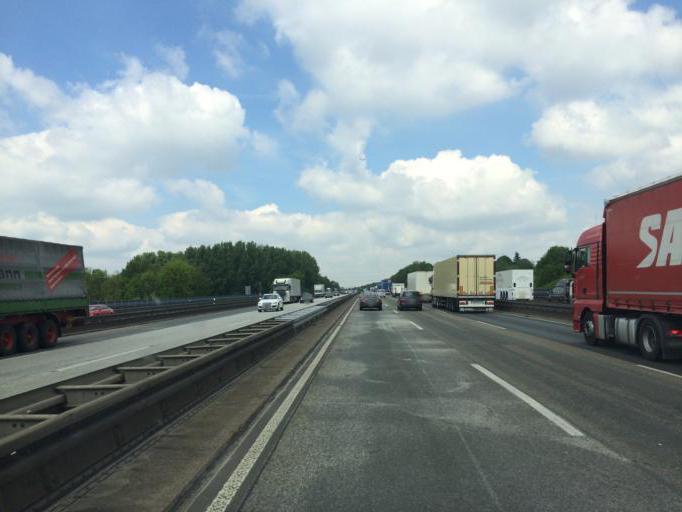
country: DE
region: North Rhine-Westphalia
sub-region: Regierungsbezirk Arnsberg
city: Holzwickede
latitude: 51.5143
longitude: 7.6545
